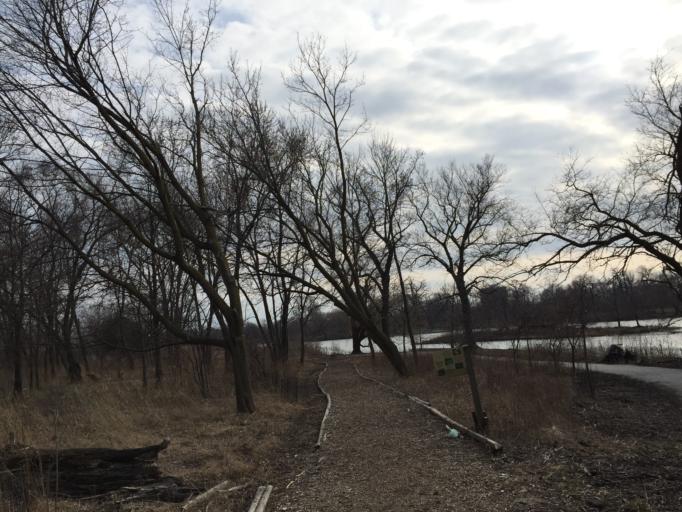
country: US
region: Illinois
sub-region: Cook County
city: Chicago
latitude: 41.7865
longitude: -87.5804
